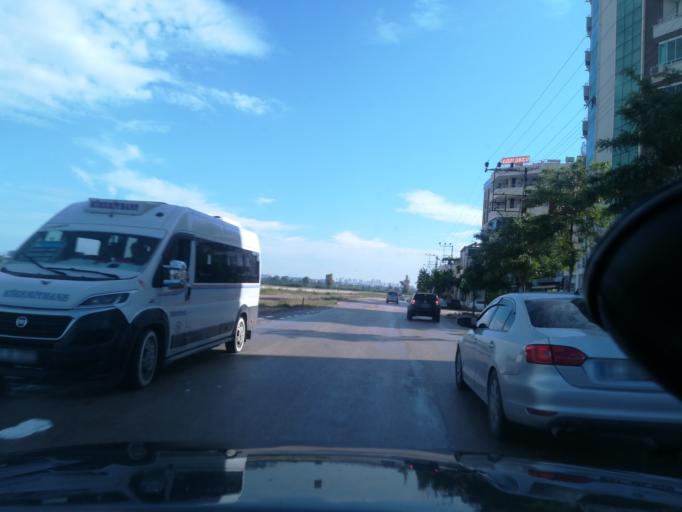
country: TR
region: Adana
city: Adana
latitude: 37.0093
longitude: 35.3575
